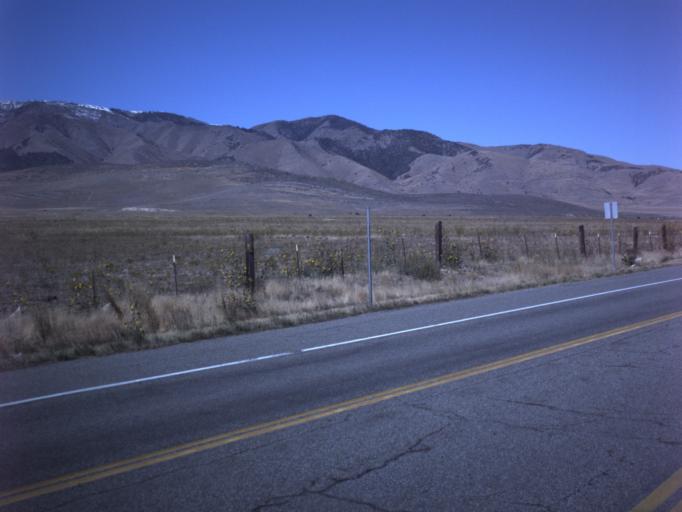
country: US
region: Utah
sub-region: Tooele County
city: Grantsville
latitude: 40.6288
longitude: -112.5114
